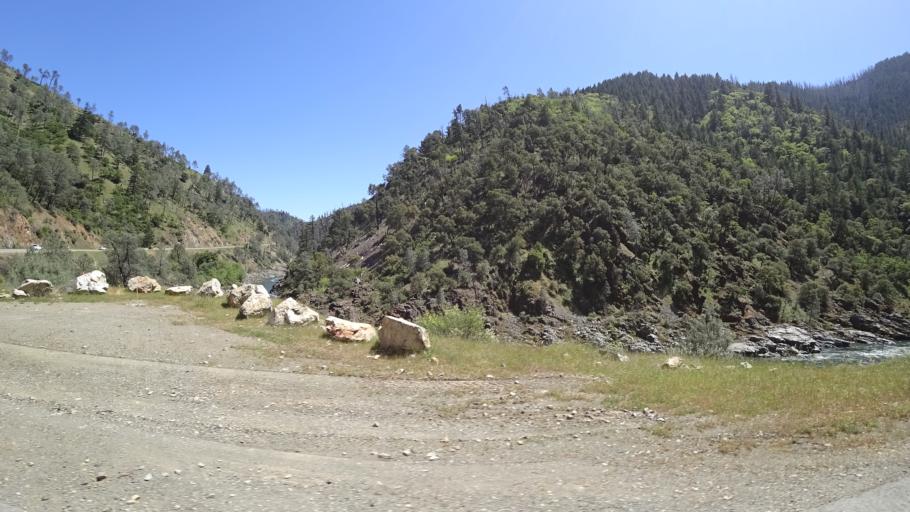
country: US
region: California
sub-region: Humboldt County
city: Willow Creek
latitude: 40.7954
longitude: -123.3680
